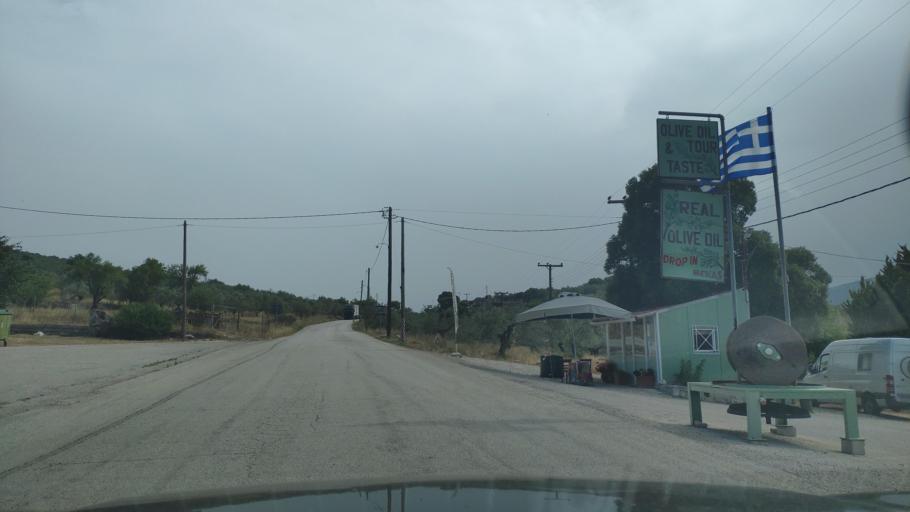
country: GR
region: Peloponnese
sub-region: Nomos Argolidos
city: Palaia Epidavros
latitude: 37.5892
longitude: 23.1577
